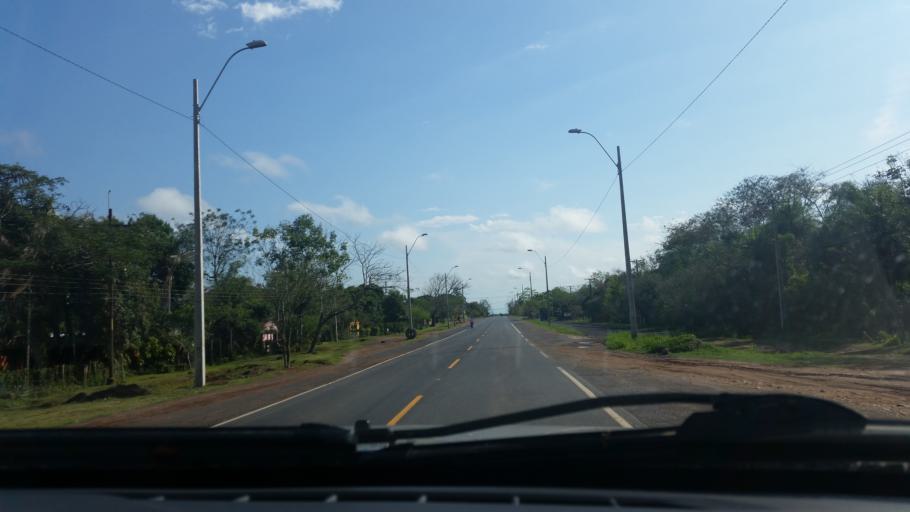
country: PY
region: Presidente Hayes
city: Benjamin Aceval
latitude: -24.9696
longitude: -57.5497
